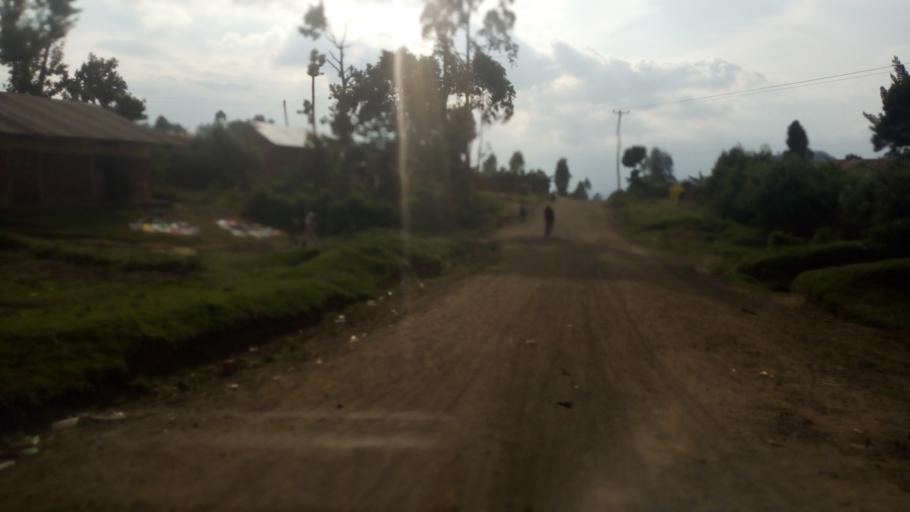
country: UG
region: Western Region
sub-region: Kisoro District
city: Kisoro
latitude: -1.2929
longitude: 29.6984
